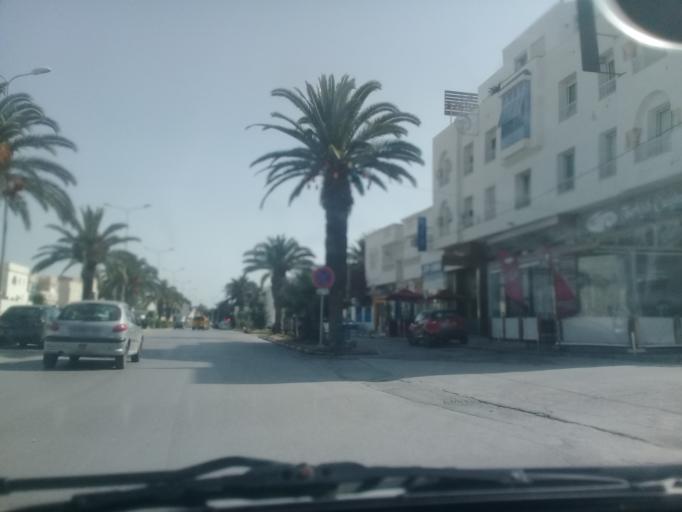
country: TN
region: Tunis
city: Al Marsa
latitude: 36.8789
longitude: 10.3273
